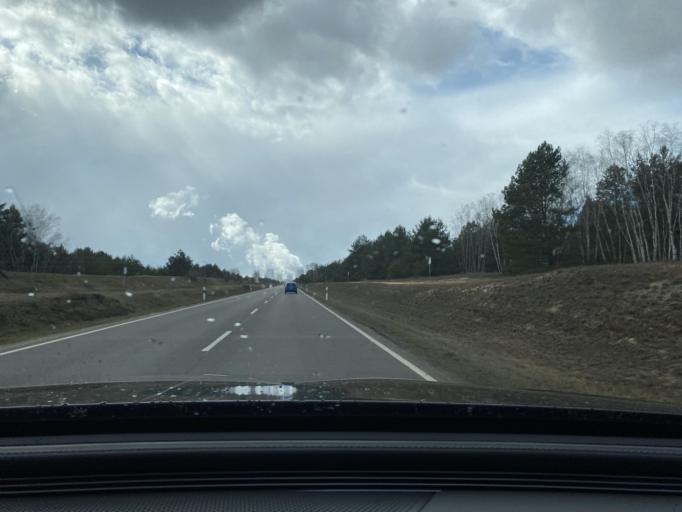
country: DE
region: Saxony
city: Weisswasser
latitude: 51.4288
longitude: 14.6527
